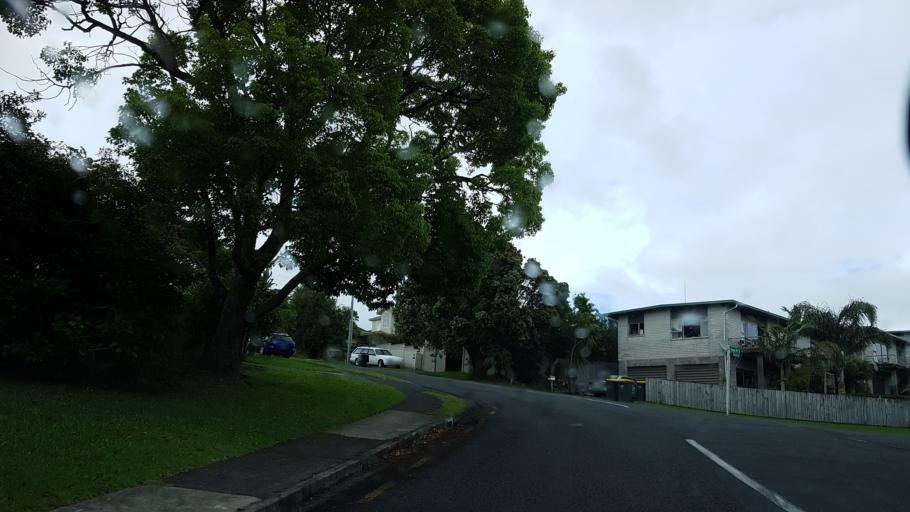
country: NZ
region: Auckland
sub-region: Auckland
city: North Shore
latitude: -36.7879
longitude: 174.7318
